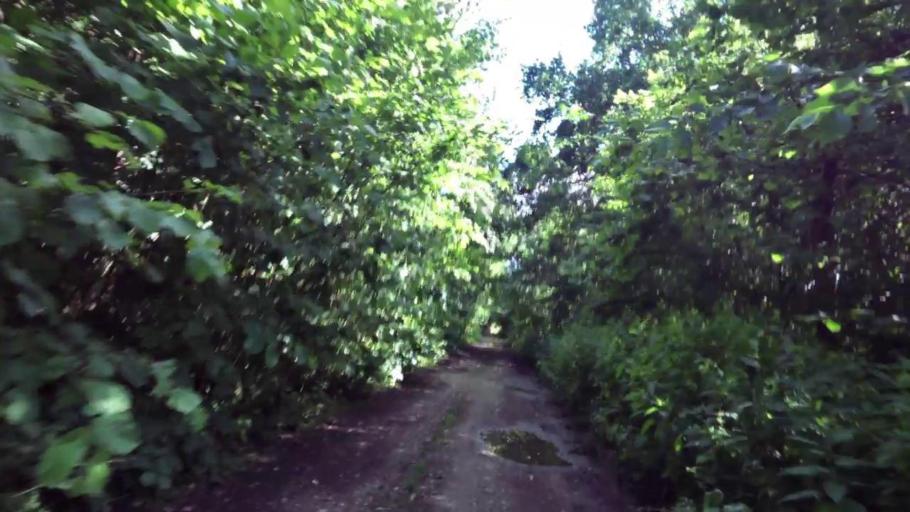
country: PL
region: West Pomeranian Voivodeship
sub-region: Powiat slawienski
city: Slawno
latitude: 54.5047
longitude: 16.7046
